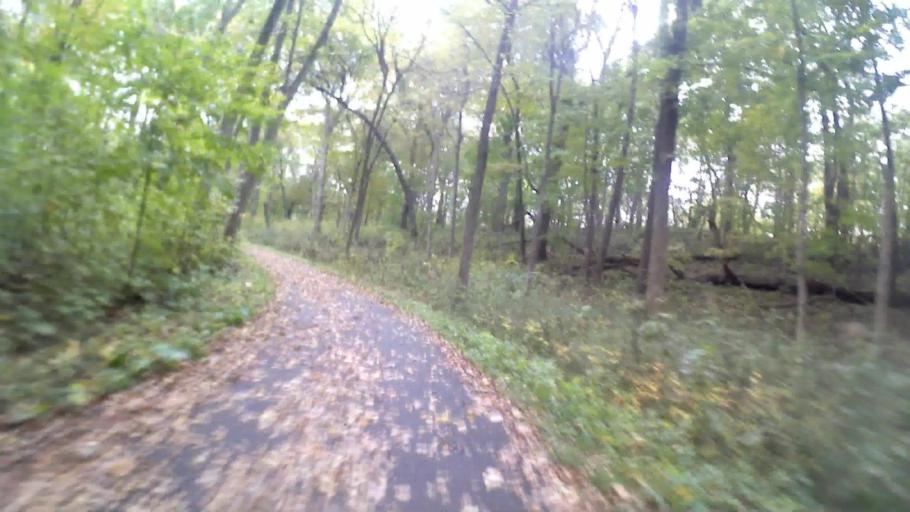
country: US
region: Illinois
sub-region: Kane County
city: Sugar Grove
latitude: 41.7822
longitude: -88.4321
